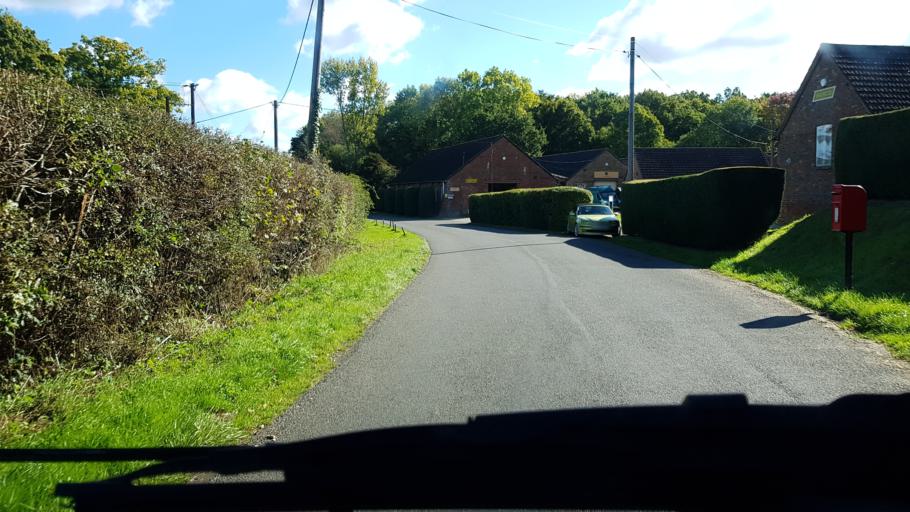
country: GB
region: England
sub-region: Surrey
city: Chiddingfold
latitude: 51.0872
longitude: -0.6065
